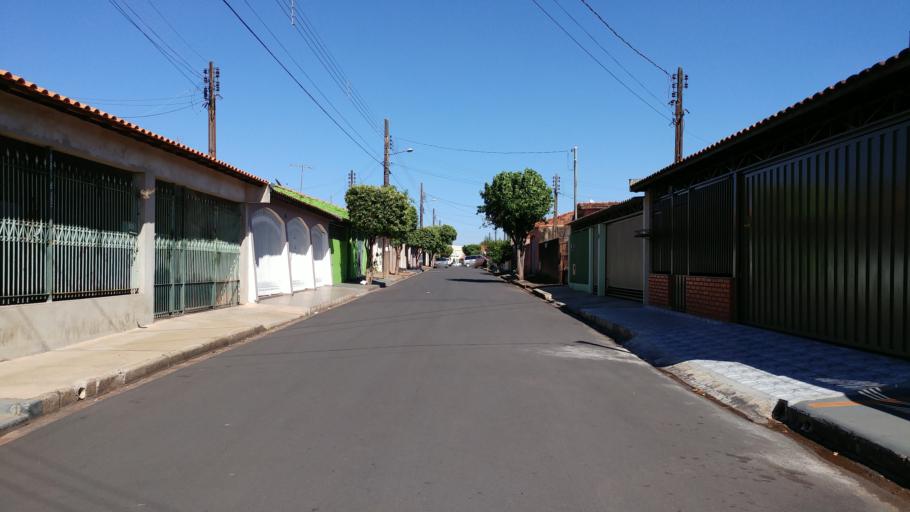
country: BR
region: Sao Paulo
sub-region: Paraguacu Paulista
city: Paraguacu Paulista
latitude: -22.4291
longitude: -50.5811
